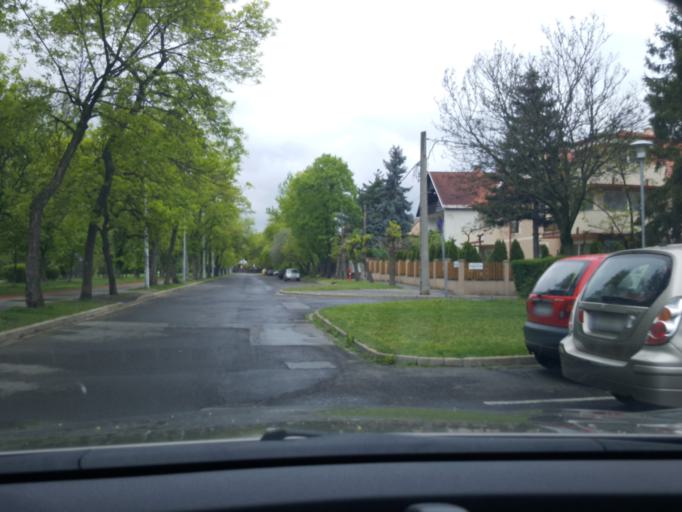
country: HU
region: Budapest
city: Budapest X. keruelet
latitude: 47.4809
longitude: 19.1471
